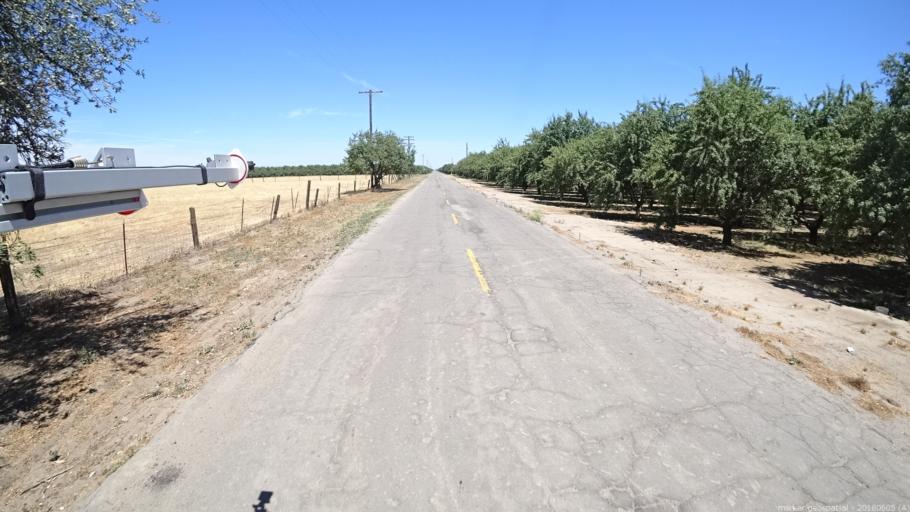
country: US
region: California
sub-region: Madera County
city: Chowchilla
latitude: 37.0907
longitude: -120.4204
